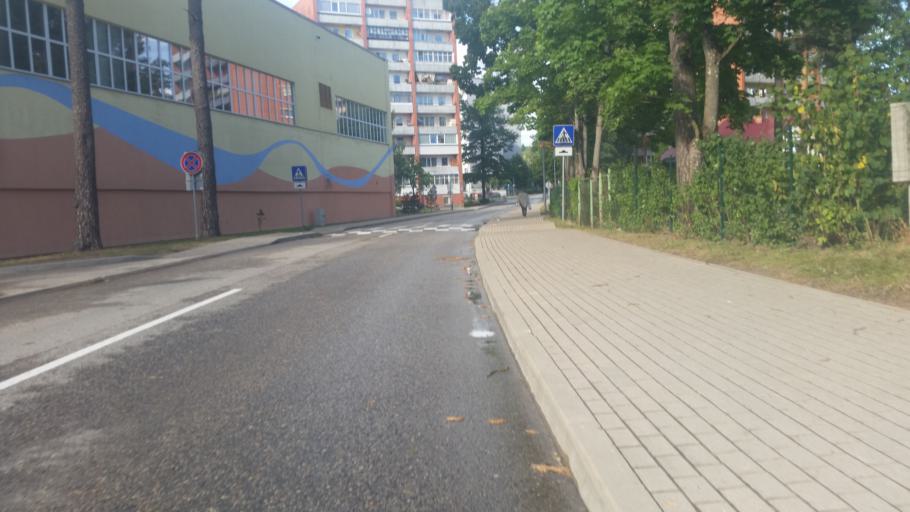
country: LV
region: Ogre
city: Ogre
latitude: 56.8214
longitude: 24.6007
